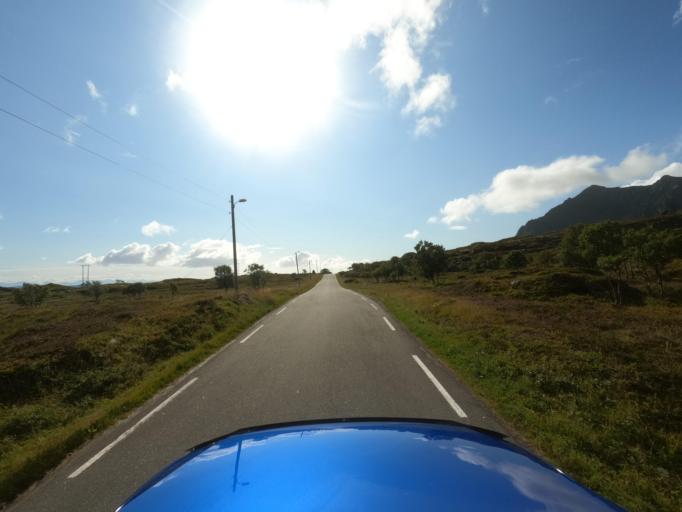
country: NO
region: Nordland
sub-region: Vestvagoy
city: Evjen
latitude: 68.2122
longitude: 14.0548
